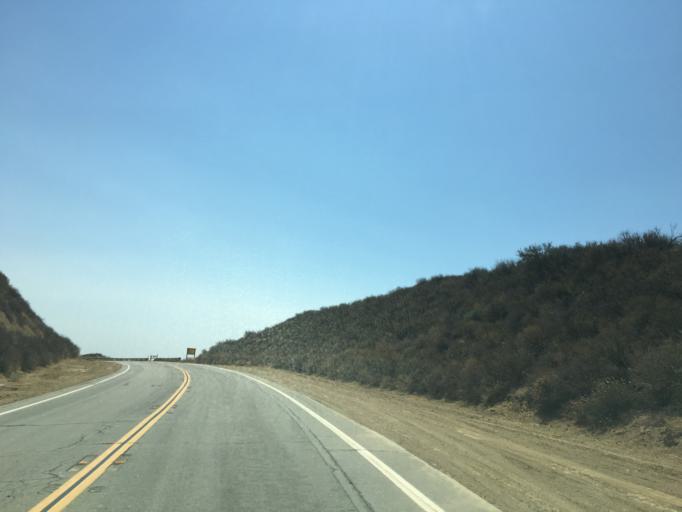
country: US
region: California
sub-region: Los Angeles County
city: Castaic
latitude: 34.5165
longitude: -118.5847
